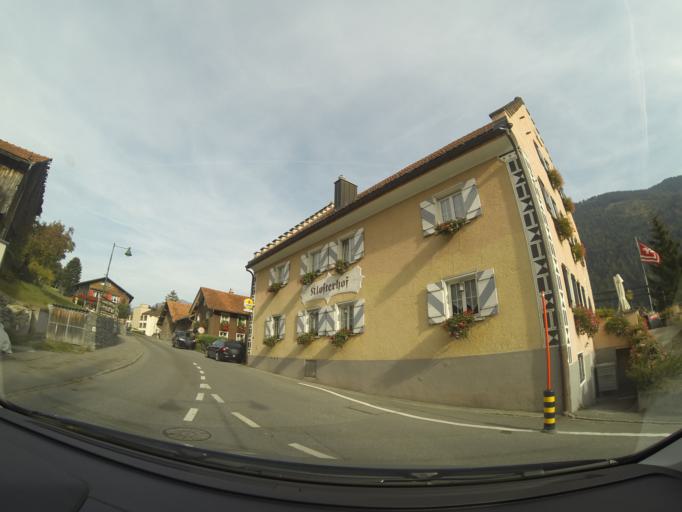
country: CH
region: Saint Gallen
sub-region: Wahlkreis Sarganserland
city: Bad Ragaz
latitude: 46.9699
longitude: 9.4808
